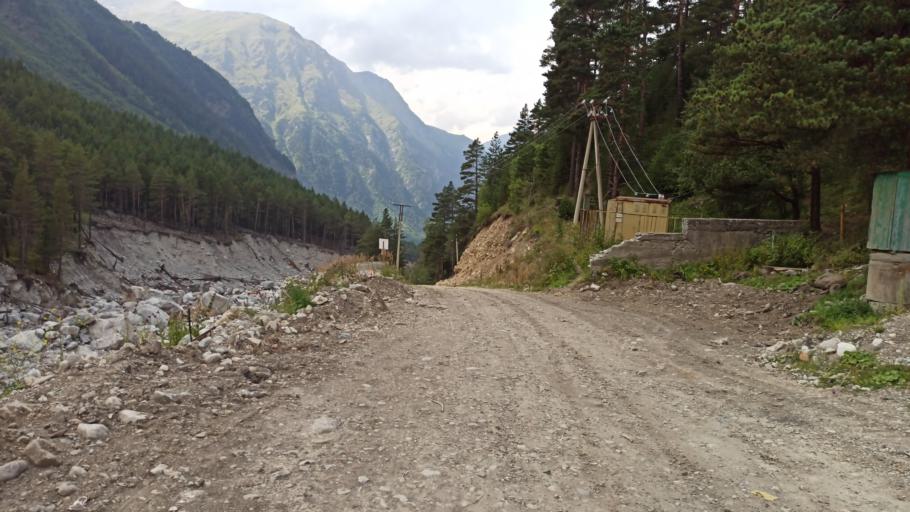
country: RU
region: Kabardino-Balkariya
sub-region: El'brusskiy Rayon
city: El'brus
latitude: 43.2194
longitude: 42.6907
